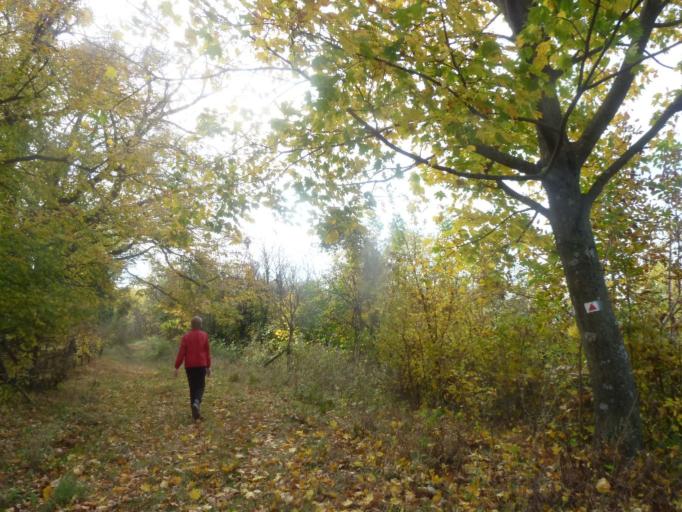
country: HU
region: Zala
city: Pacsa
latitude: 46.5953
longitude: 17.0534
